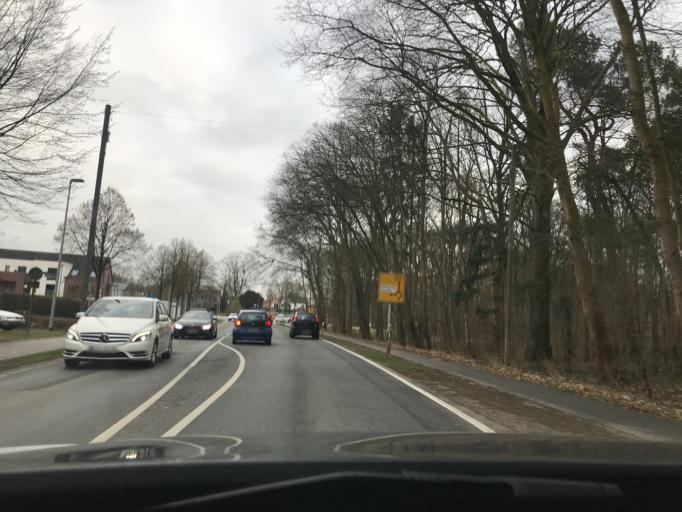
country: DE
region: North Rhine-Westphalia
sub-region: Regierungsbezirk Dusseldorf
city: Kleve
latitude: 51.7626
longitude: 6.1846
